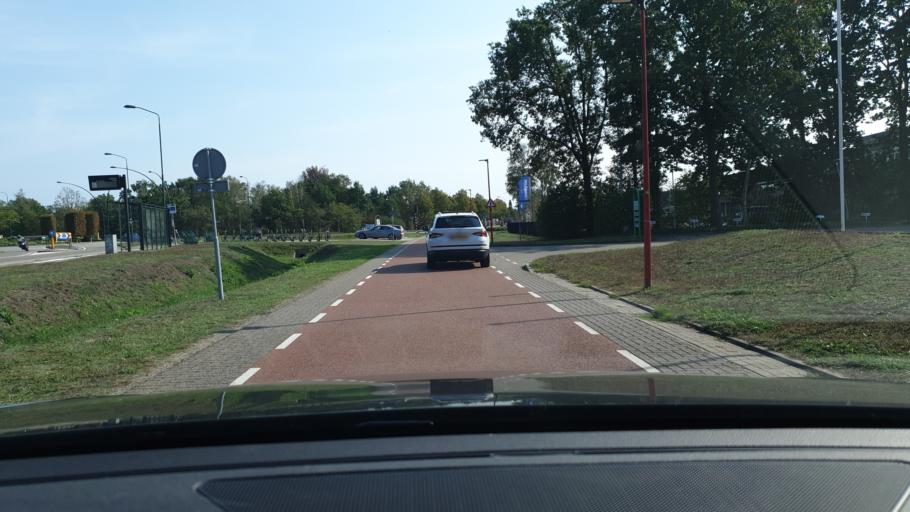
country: NL
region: North Brabant
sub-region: Gemeente Bernheze
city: Heesch
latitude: 51.7153
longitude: 5.5568
